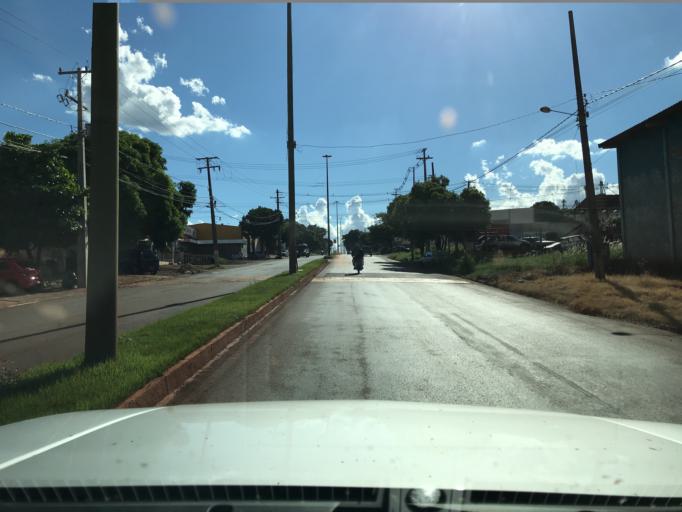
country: BR
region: Parana
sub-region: Palotina
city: Palotina
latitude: -24.2792
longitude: -53.8253
